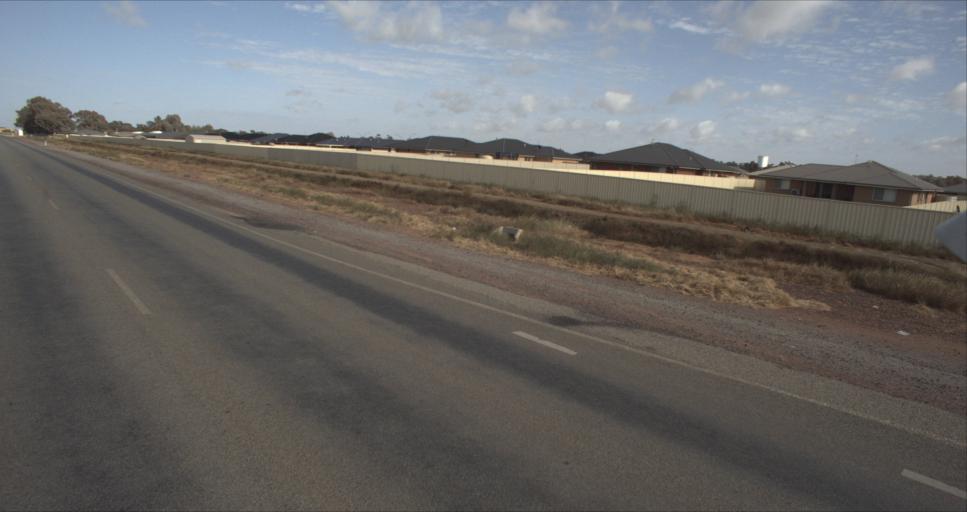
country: AU
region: New South Wales
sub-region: Leeton
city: Leeton
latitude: -34.5711
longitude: 146.4018
